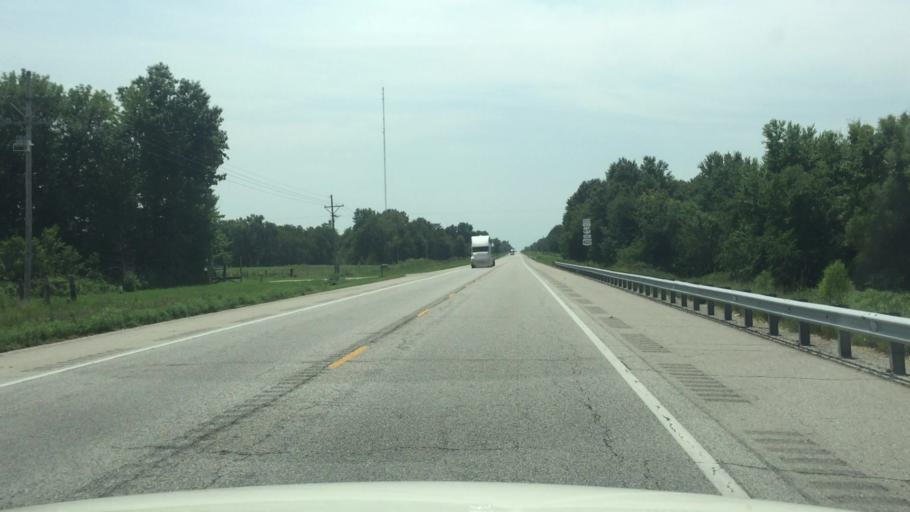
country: US
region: Kansas
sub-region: Cherokee County
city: Galena
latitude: 37.1323
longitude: -94.7044
